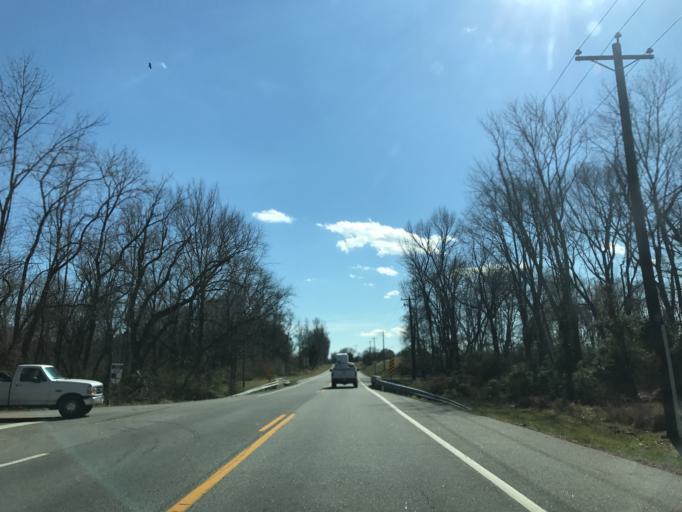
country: US
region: Maryland
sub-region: Kent County
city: Rock Hall
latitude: 39.1823
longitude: -76.1949
